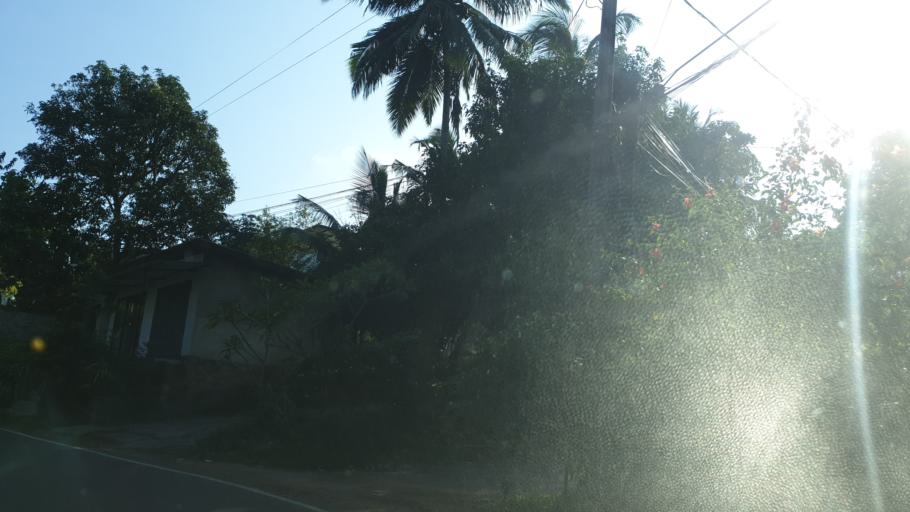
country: LK
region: Western
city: Battaramulla South
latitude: 6.8881
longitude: 79.9434
